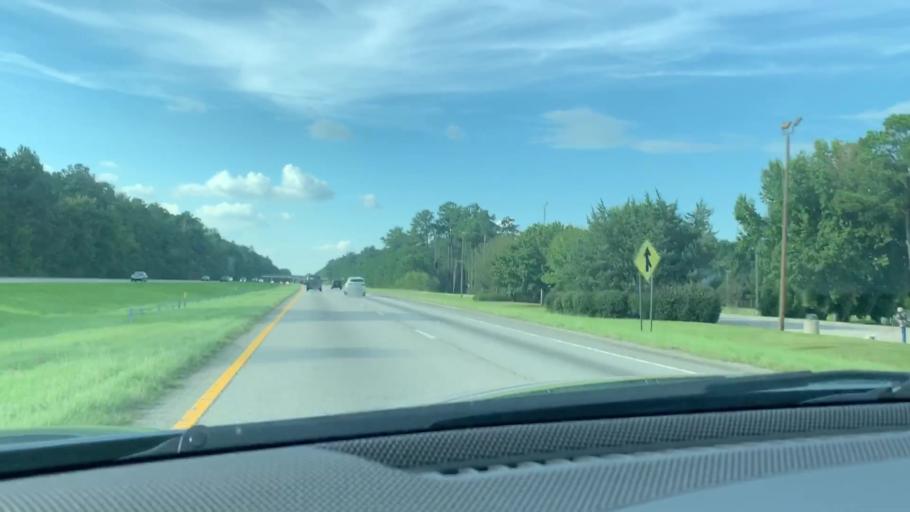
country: US
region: South Carolina
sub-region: Orangeburg County
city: Brookdale
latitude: 33.4809
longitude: -80.7563
